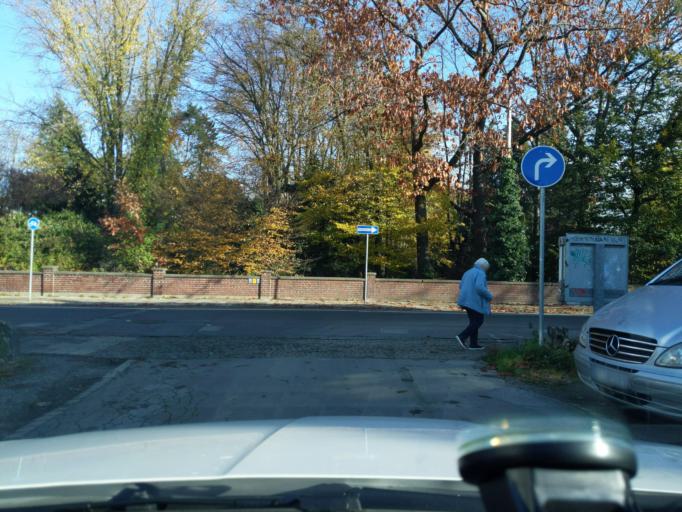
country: DE
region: North Rhine-Westphalia
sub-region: Regierungsbezirk Dusseldorf
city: Willich
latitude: 51.2653
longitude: 6.5451
